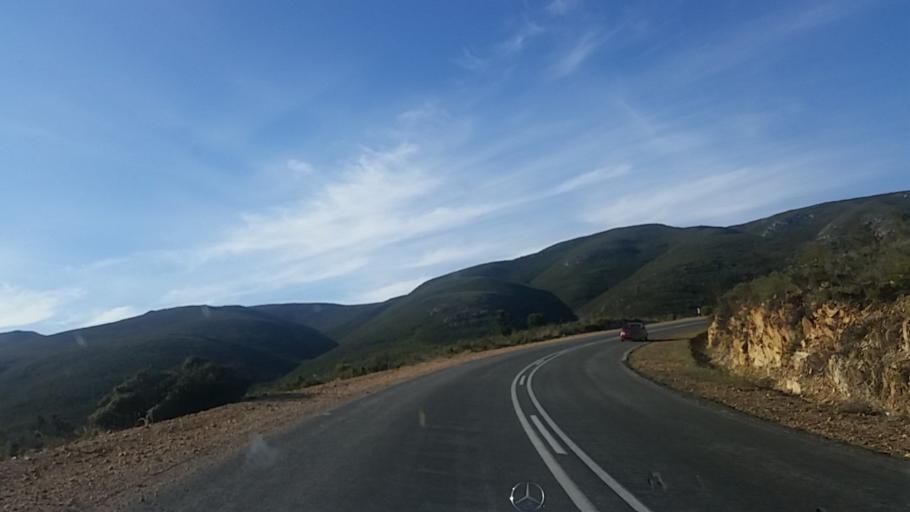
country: ZA
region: Western Cape
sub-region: Eden District Municipality
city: Knysna
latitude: -33.7551
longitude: 22.9451
